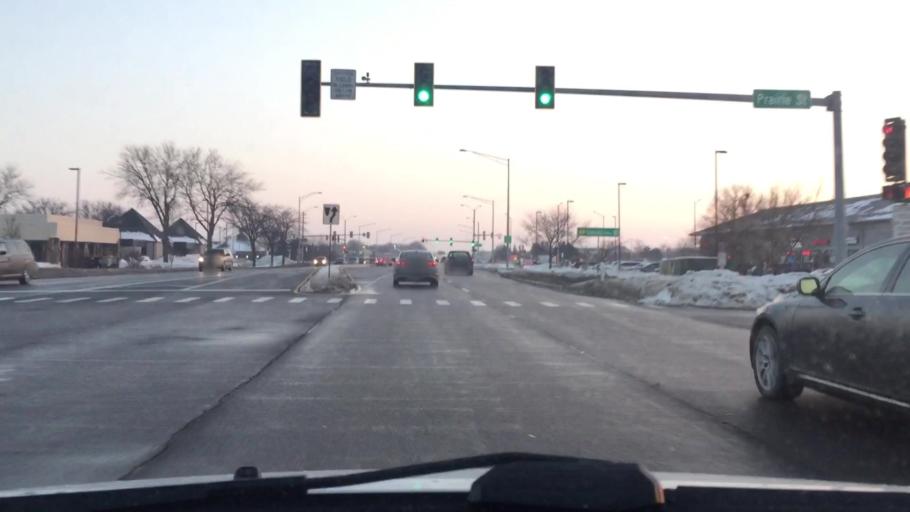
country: US
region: Illinois
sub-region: Kane County
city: Saint Charles
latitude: 41.9038
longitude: -88.3399
